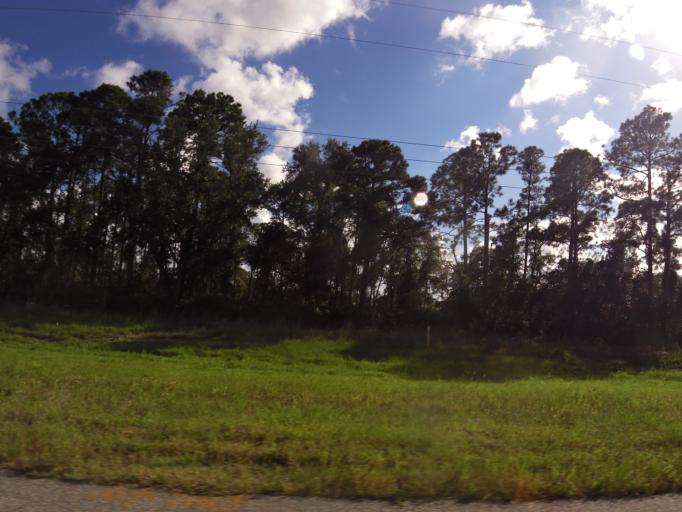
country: US
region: Georgia
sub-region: Glynn County
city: Brunswick
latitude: 31.1235
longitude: -81.5468
